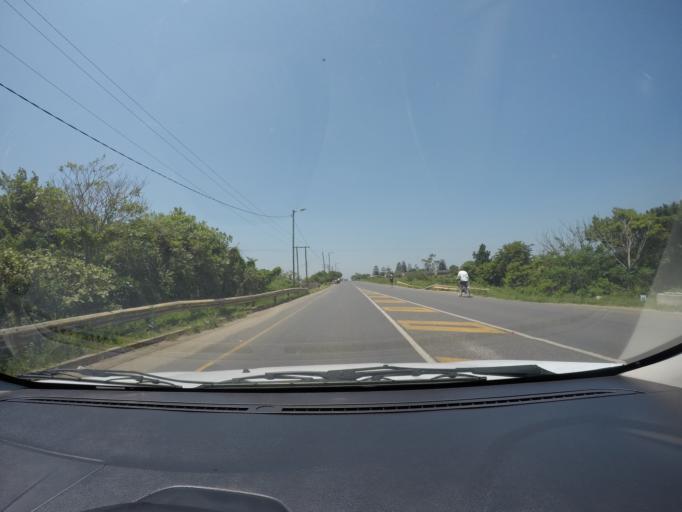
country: ZA
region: KwaZulu-Natal
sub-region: uThungulu District Municipality
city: eSikhawini
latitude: -28.8782
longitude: 31.8927
